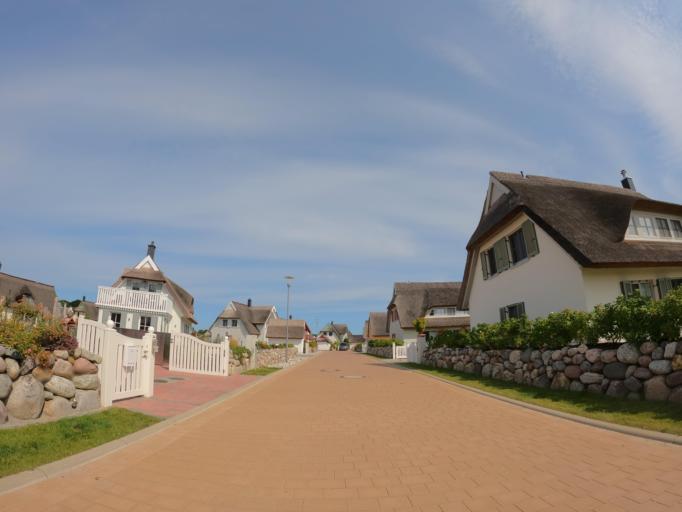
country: DE
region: Mecklenburg-Vorpommern
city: Kramerhof
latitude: 54.3520
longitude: 13.0765
